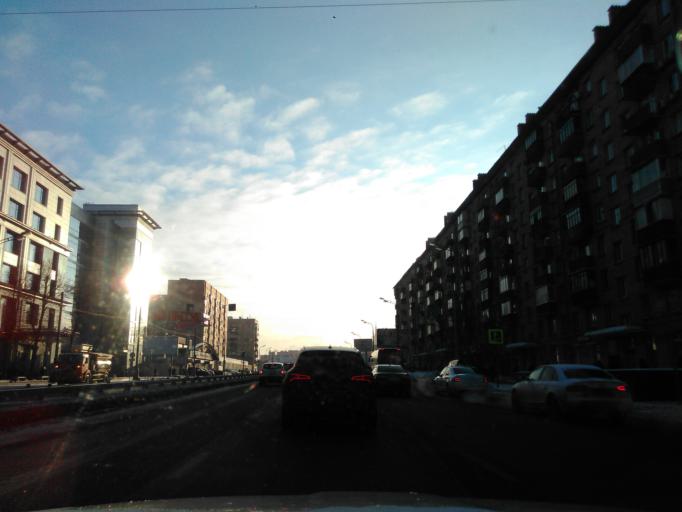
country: RU
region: Moskovskaya
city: Presnenskiy
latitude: 55.7640
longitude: 37.5553
